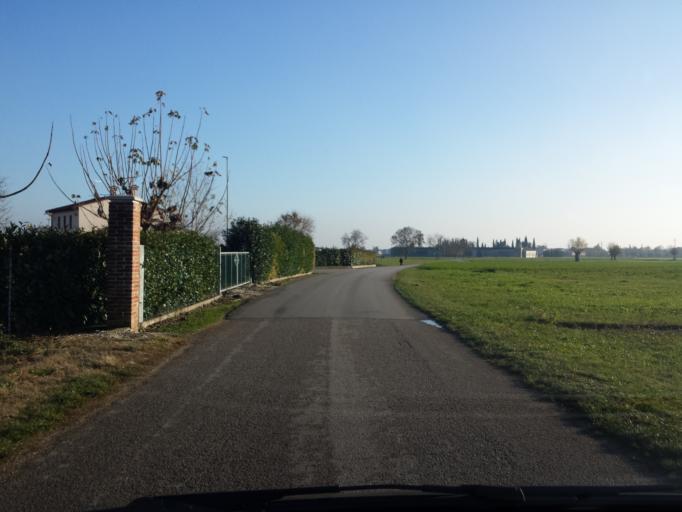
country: IT
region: Veneto
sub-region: Provincia di Vicenza
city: Sandrigo
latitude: 45.6739
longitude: 11.5914
